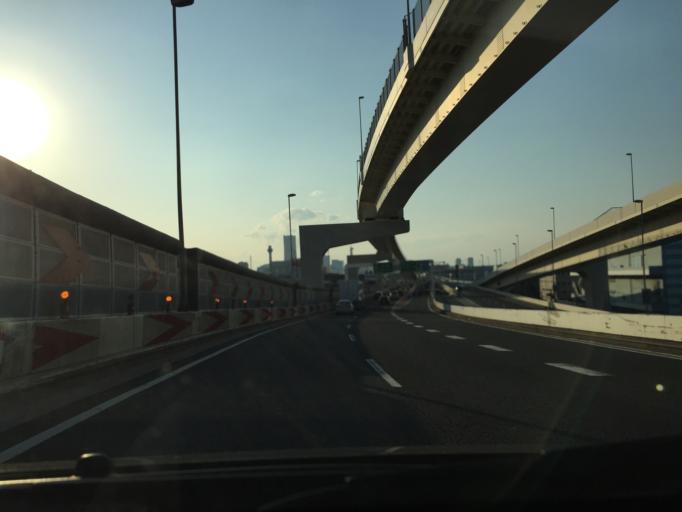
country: JP
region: Kanagawa
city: Yokohama
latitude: 35.4376
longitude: 139.6640
